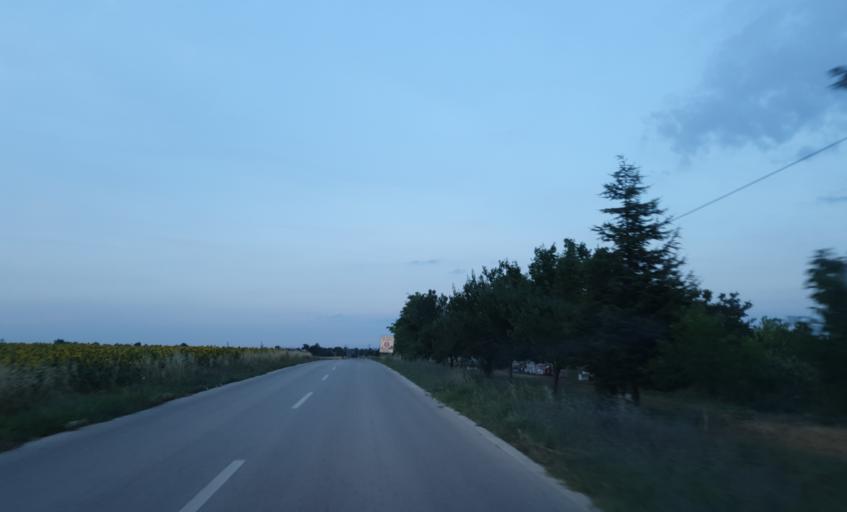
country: TR
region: Tekirdag
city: Beyazkoy
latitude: 41.4317
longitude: 27.6884
